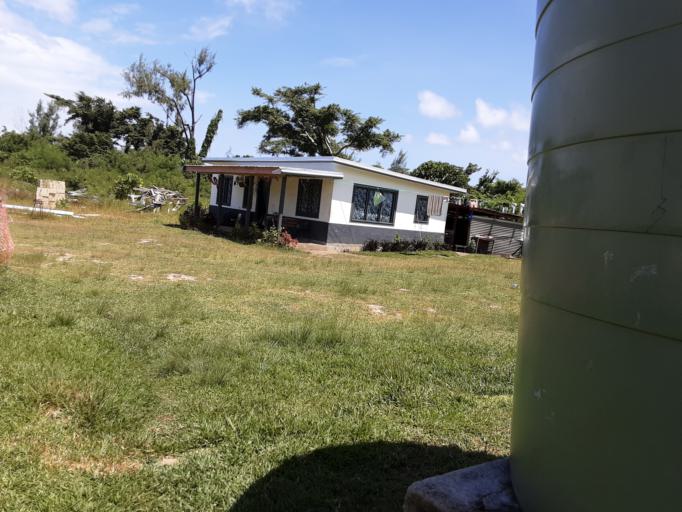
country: VU
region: Sanma
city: Luganville
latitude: -15.5214
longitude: 167.2523
